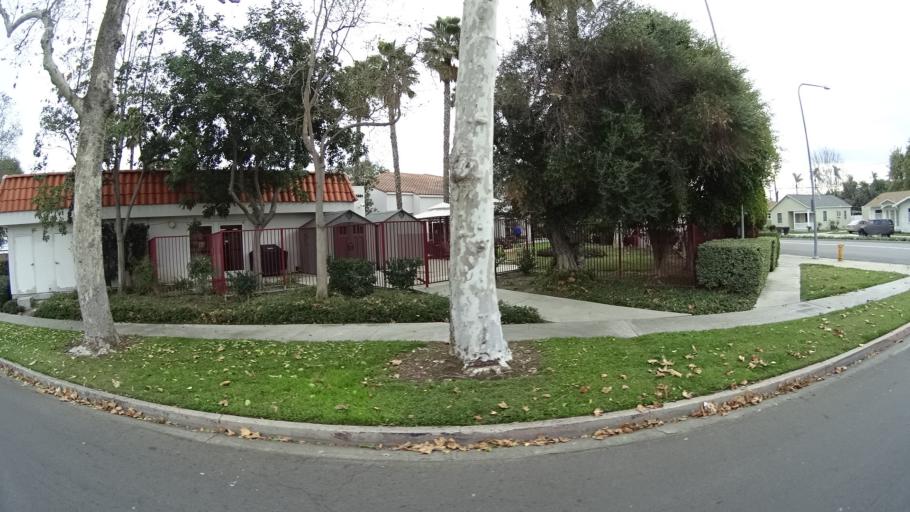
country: US
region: California
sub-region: Orange County
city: Garden Grove
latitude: 33.7763
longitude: -117.9344
